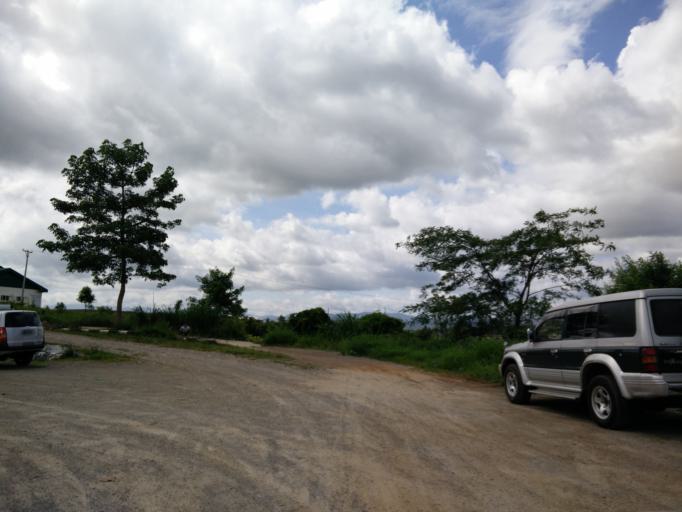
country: MM
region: Shan
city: Lashio
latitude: 23.0307
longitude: 97.7730
